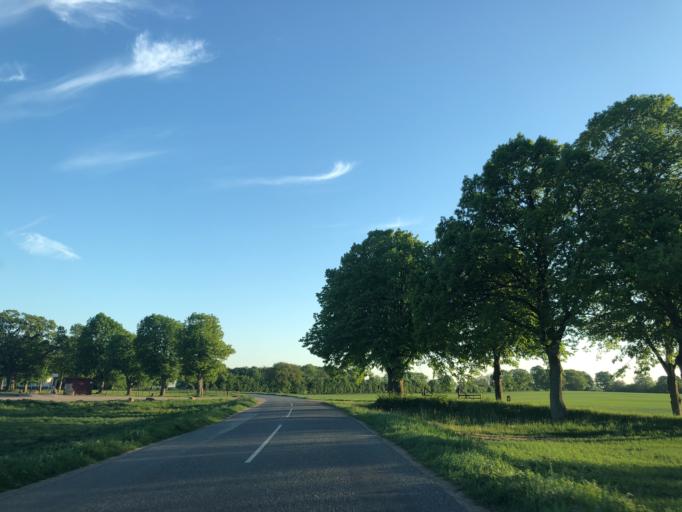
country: DK
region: Zealand
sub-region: Koge Kommune
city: Borup
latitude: 55.4209
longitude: 11.9328
